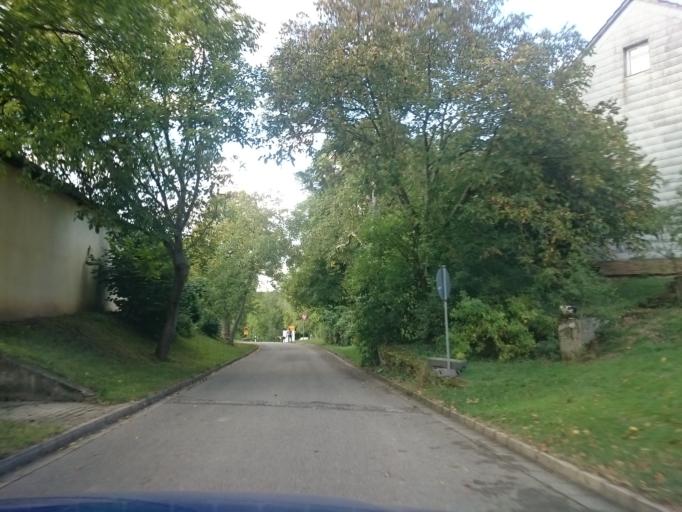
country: DE
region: Bavaria
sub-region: Regierungsbezirk Mittelfranken
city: Heideck
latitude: 49.1288
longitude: 11.1792
